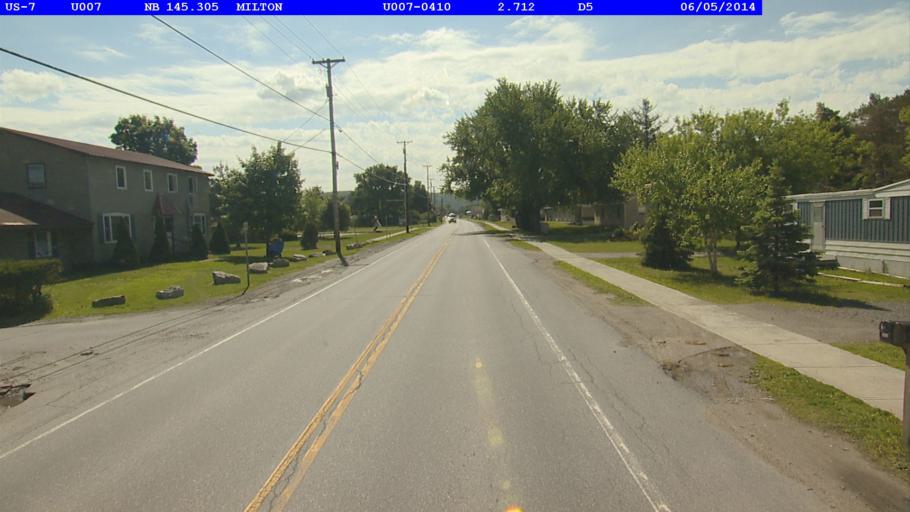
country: US
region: Vermont
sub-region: Chittenden County
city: Milton
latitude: 44.6265
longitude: -73.1394
